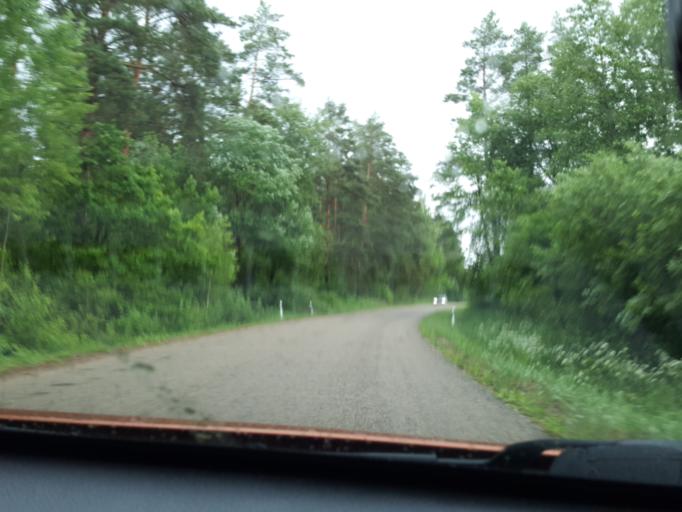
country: LV
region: Ikskile
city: Ikskile
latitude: 56.8893
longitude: 24.4969
